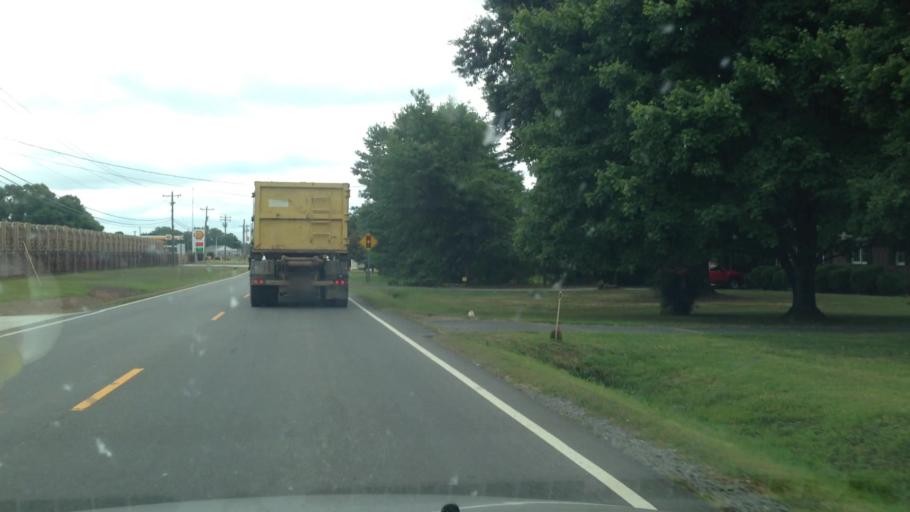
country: US
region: North Carolina
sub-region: Rockingham County
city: Wentworth
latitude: 36.3695
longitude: -79.7240
